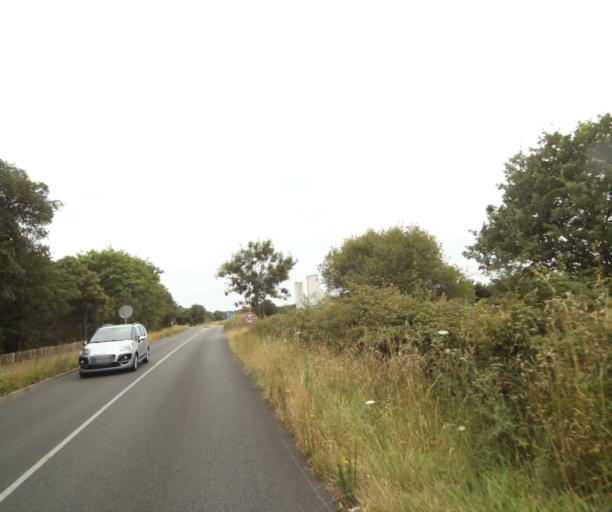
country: FR
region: Pays de la Loire
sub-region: Departement de la Vendee
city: Chateau-d'Olonne
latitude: 46.4633
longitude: -1.7220
